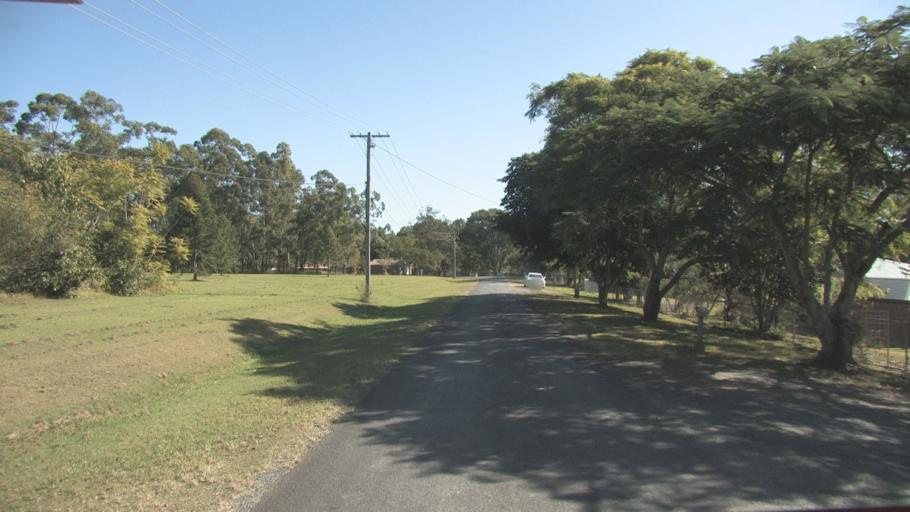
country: AU
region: Queensland
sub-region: Logan
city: Logan Reserve
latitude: -27.7343
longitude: 153.1173
